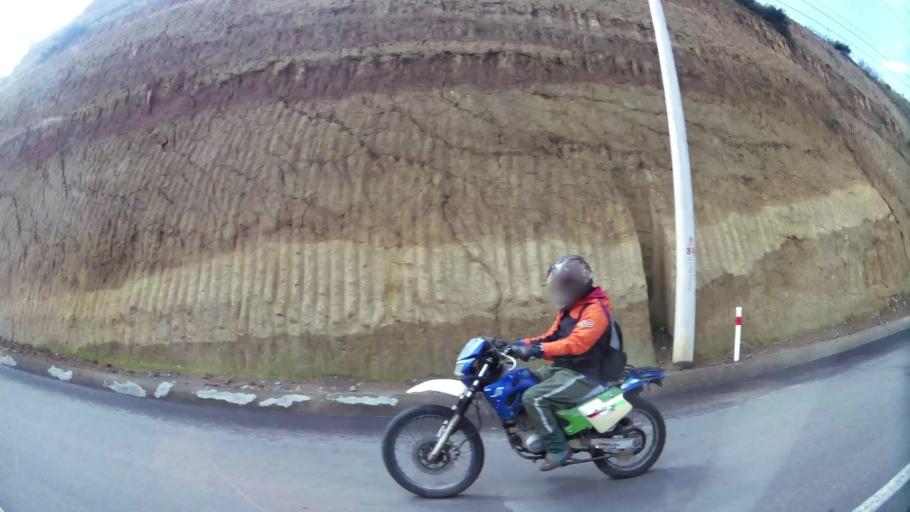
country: EC
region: Pichincha
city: Sangolqui
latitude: -0.3237
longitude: -78.4011
